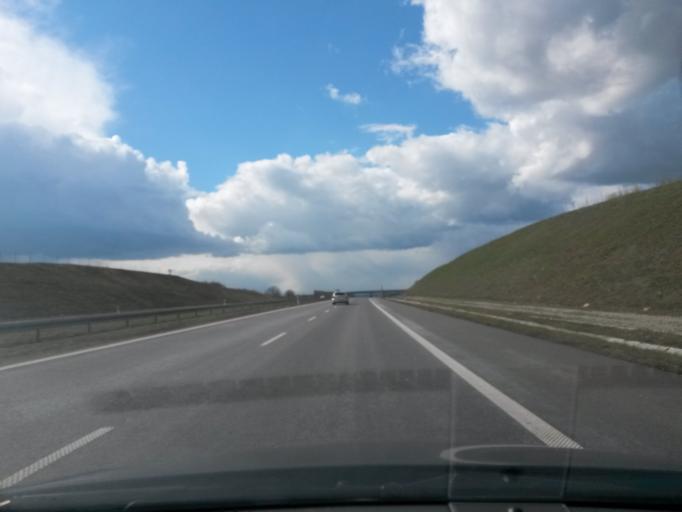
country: PL
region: Greater Poland Voivodeship
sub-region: Powiat kolski
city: Koscielec
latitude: 52.1434
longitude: 18.5225
